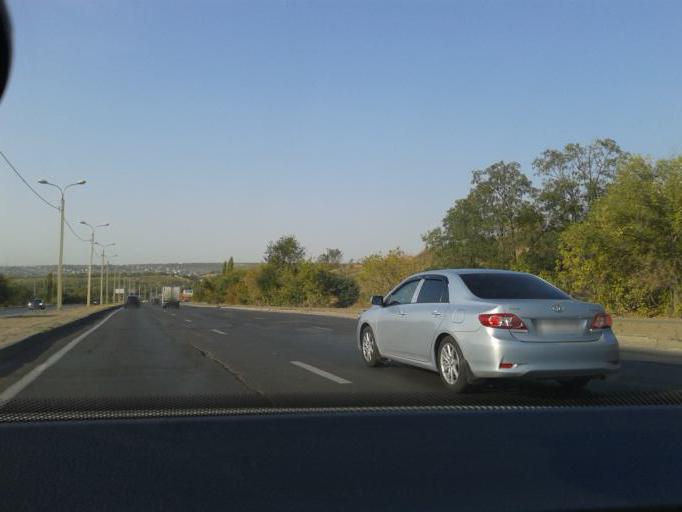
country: RU
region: Volgograd
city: Volgograd
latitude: 48.7368
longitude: 44.4583
